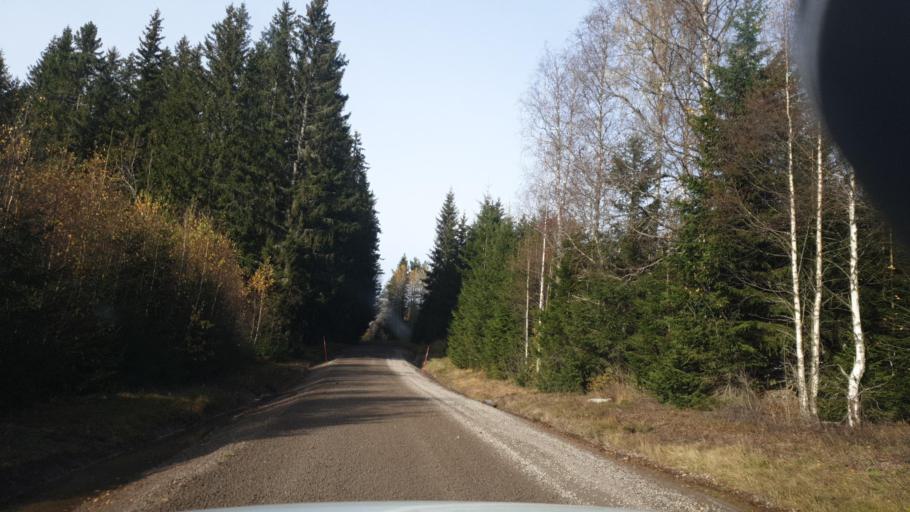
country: NO
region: Hedmark
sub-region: Eidskog
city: Skotterud
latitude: 59.7339
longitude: 12.0951
